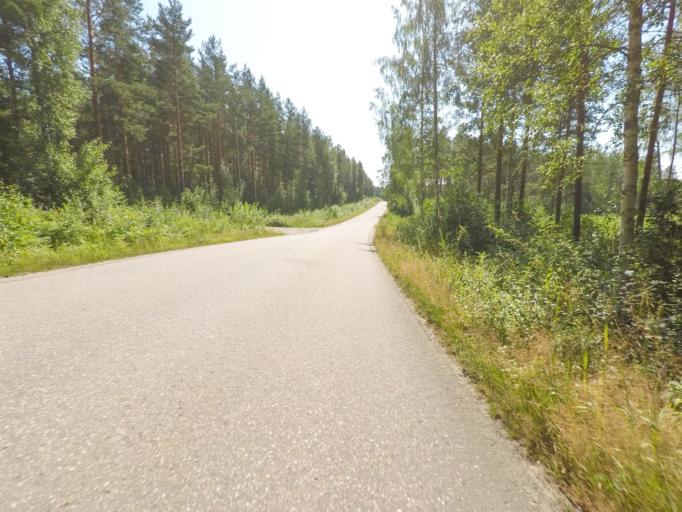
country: FI
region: Southern Savonia
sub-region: Mikkeli
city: Puumala
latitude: 61.4421
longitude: 28.1646
